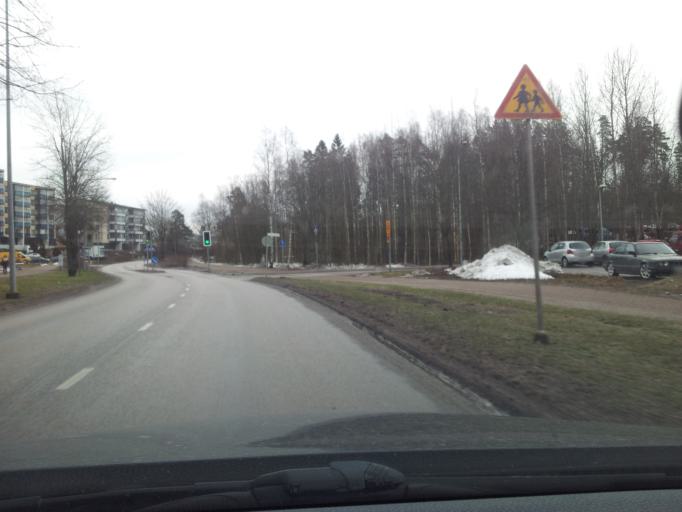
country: FI
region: Uusimaa
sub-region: Helsinki
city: Espoo
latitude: 60.1994
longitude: 24.6653
